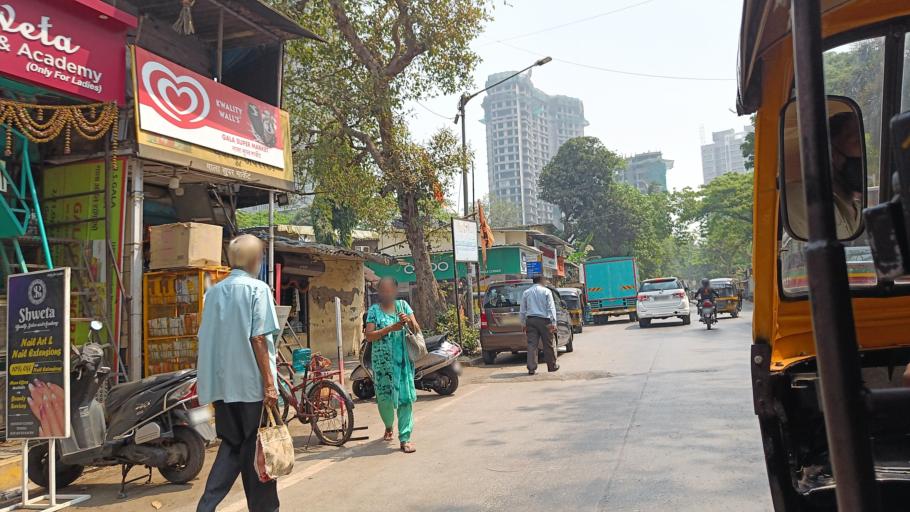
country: IN
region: Maharashtra
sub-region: Mumbai Suburban
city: Powai
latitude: 19.1533
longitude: 72.8414
